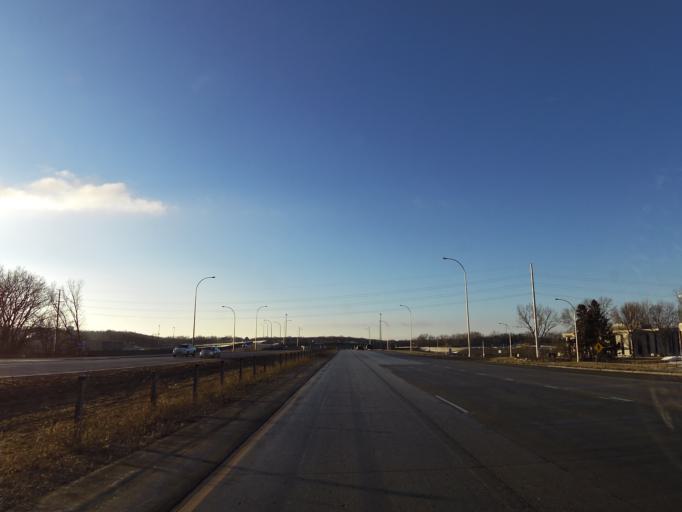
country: US
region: Minnesota
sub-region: Hennepin County
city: Edina
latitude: 44.8639
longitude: -93.3963
